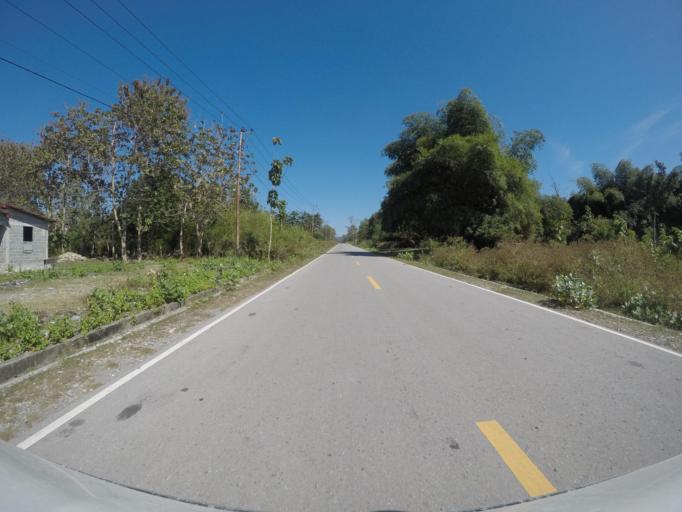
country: TL
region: Viqueque
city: Viqueque
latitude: -8.9739
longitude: 126.0367
